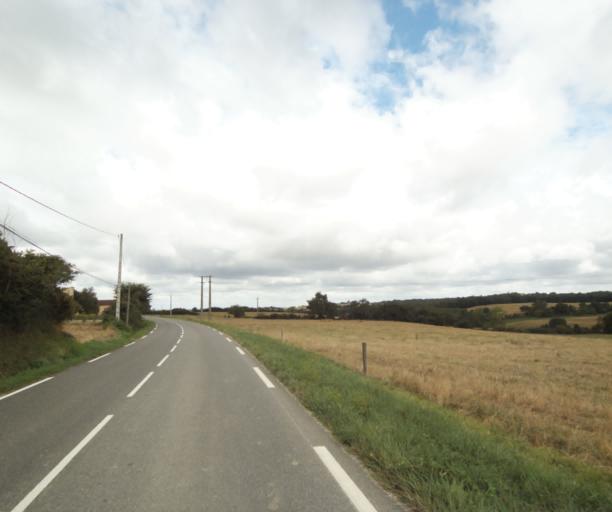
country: FR
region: Midi-Pyrenees
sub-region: Departement de la Haute-Garonne
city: Flourens
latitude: 43.5980
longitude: 1.5371
